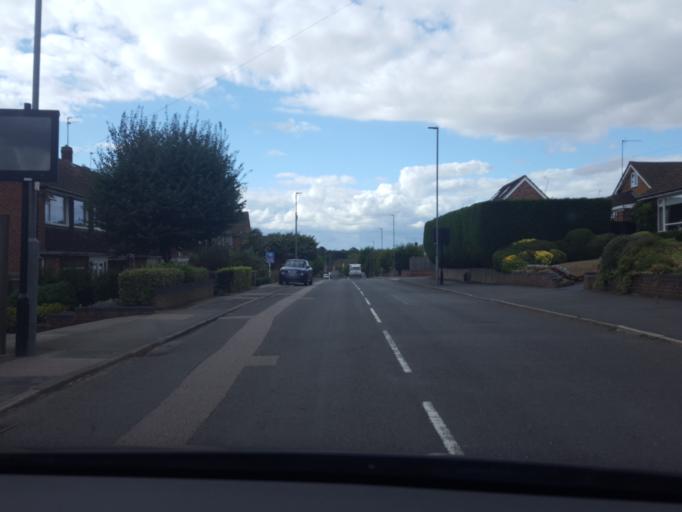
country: GB
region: England
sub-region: Leicestershire
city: Loughborough
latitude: 52.7542
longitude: -1.2237
